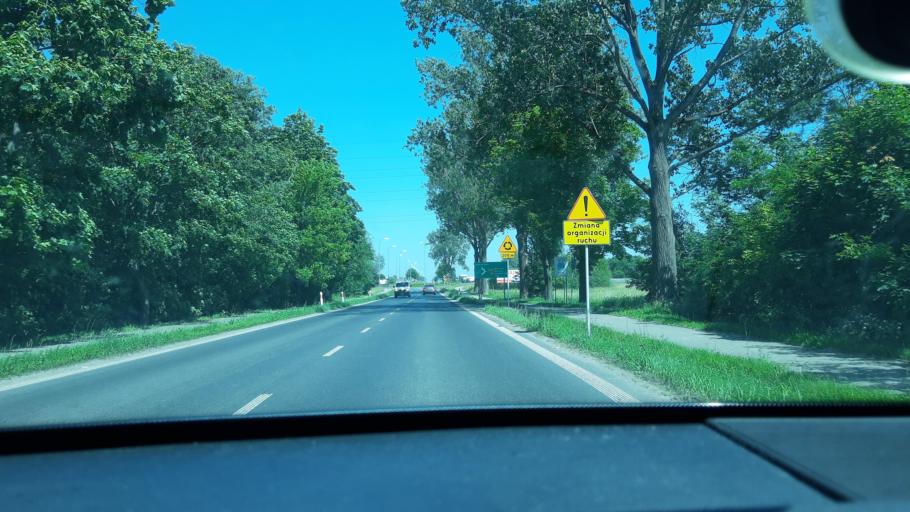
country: PL
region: Lodz Voivodeship
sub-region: Powiat zdunskowolski
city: Zapolice
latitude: 51.6066
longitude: 18.8724
